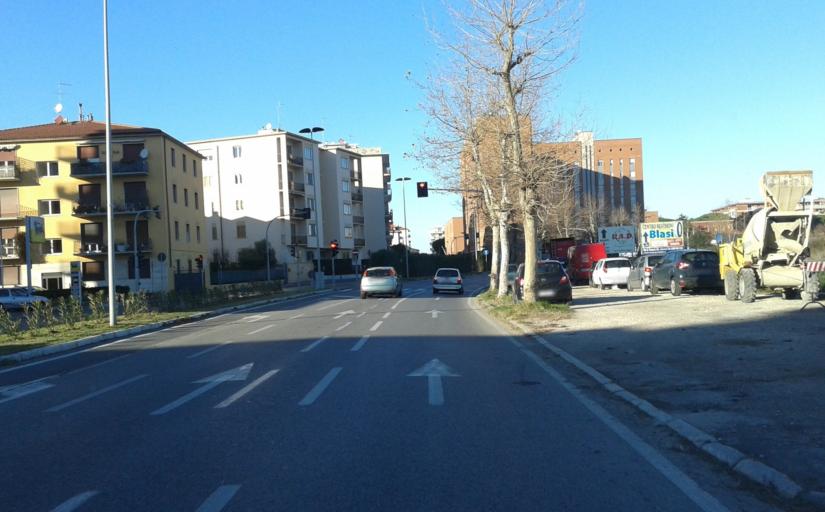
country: IT
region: Tuscany
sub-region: Provincia di Livorno
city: Livorno
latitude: 43.5367
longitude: 10.3230
